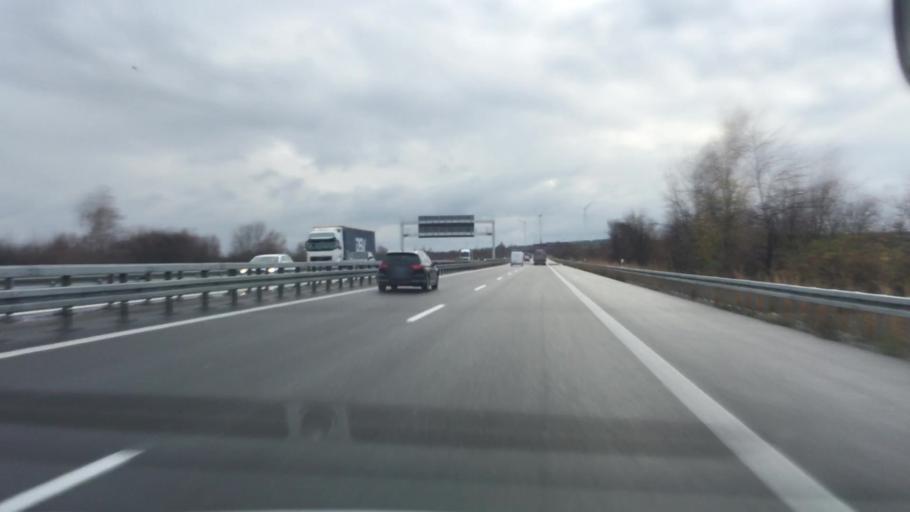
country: DE
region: Saxony-Anhalt
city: Ilberstedt
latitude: 51.7914
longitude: 11.6779
